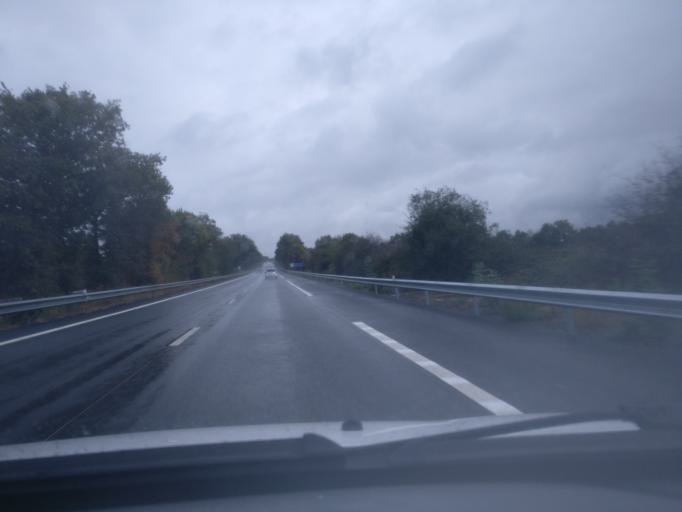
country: FR
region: Brittany
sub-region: Departement d'Ille-et-Vilaine
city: Grand-Fougeray
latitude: 47.7144
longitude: -1.7072
